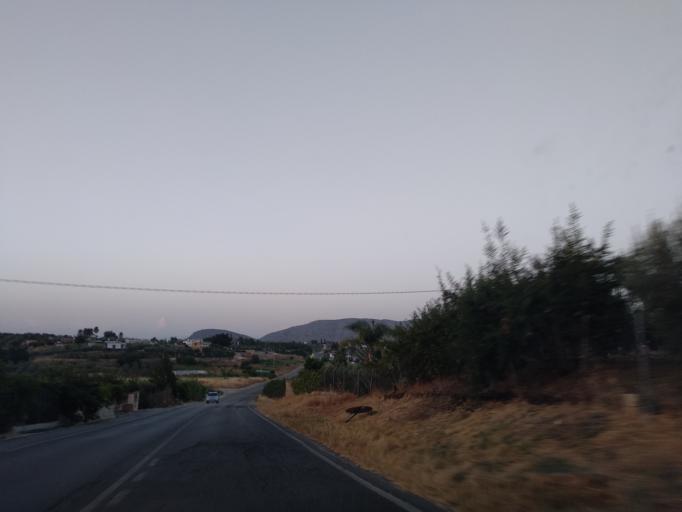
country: ES
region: Andalusia
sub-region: Provincia de Malaga
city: Alhaurin el Grande
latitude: 36.6700
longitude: -4.6659
